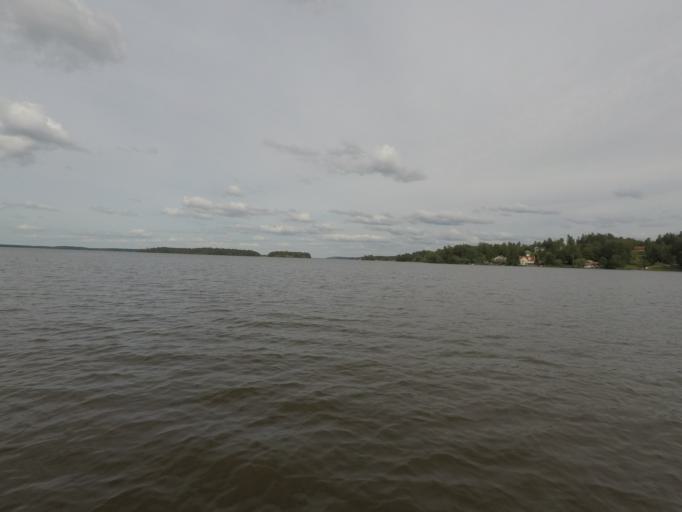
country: SE
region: Soedermanland
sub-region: Eskilstuna Kommun
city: Kvicksund
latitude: 59.4545
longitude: 16.3405
